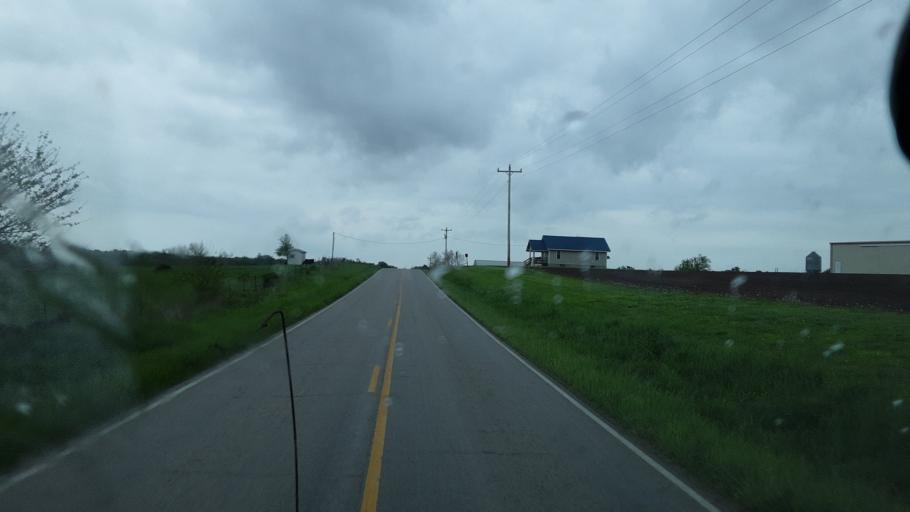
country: US
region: Missouri
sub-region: Boone County
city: Centralia
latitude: 39.4008
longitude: -92.2104
